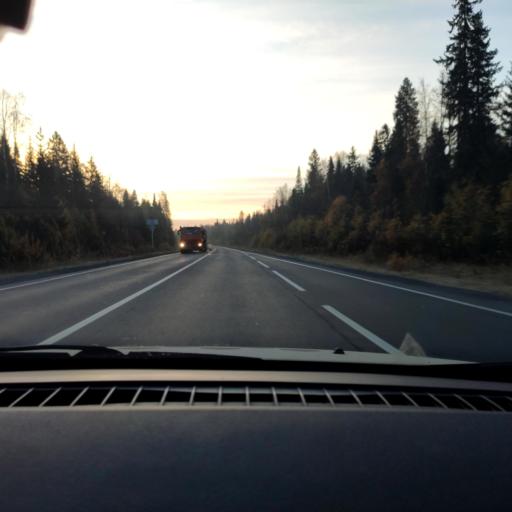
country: RU
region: Perm
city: Novyye Lyady
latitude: 58.0324
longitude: 56.4815
